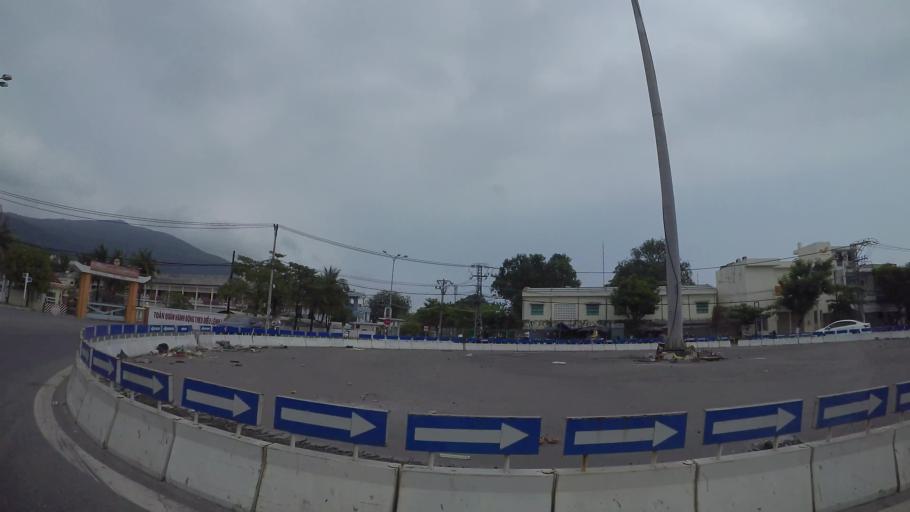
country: VN
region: Da Nang
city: Da Nang
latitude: 16.1018
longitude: 108.2474
